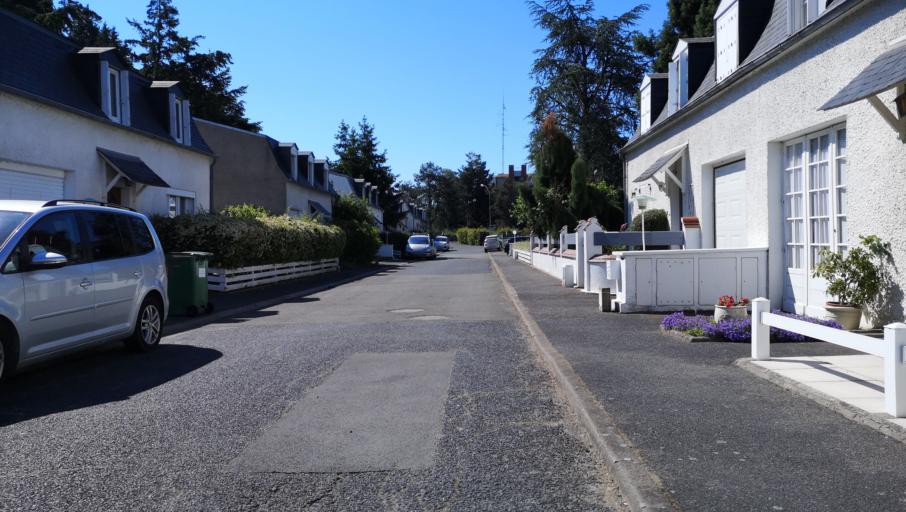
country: FR
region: Centre
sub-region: Departement du Loiret
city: Orleans
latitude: 47.8888
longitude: 1.8927
